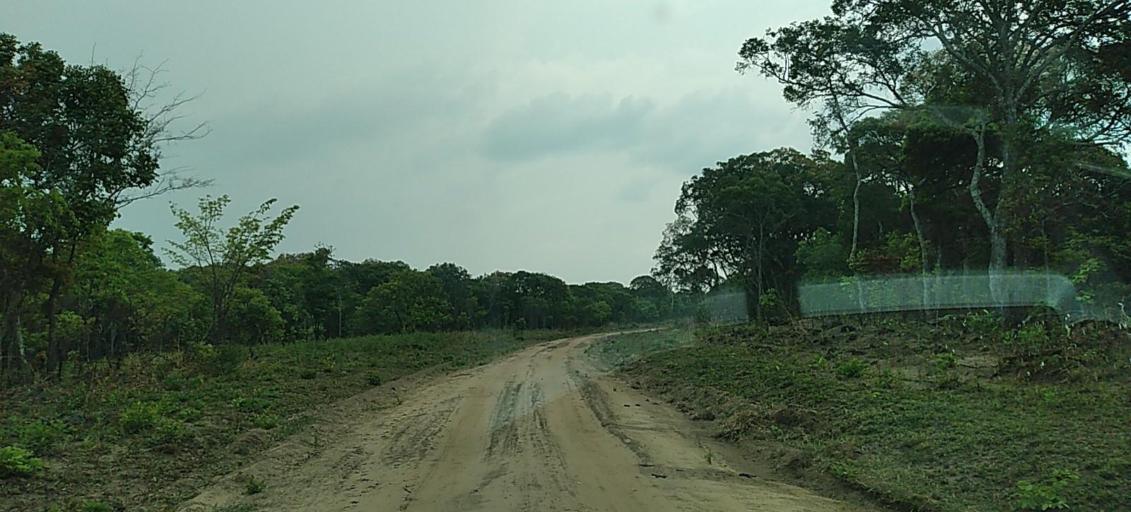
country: ZM
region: North-Western
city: Mwinilunga
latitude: -11.4105
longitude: 24.6187
